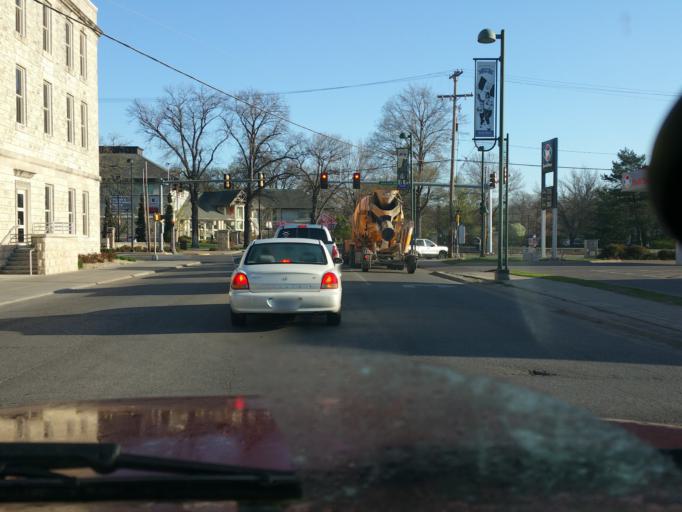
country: US
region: Kansas
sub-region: Riley County
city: Manhattan
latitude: 39.1856
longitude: -96.5783
